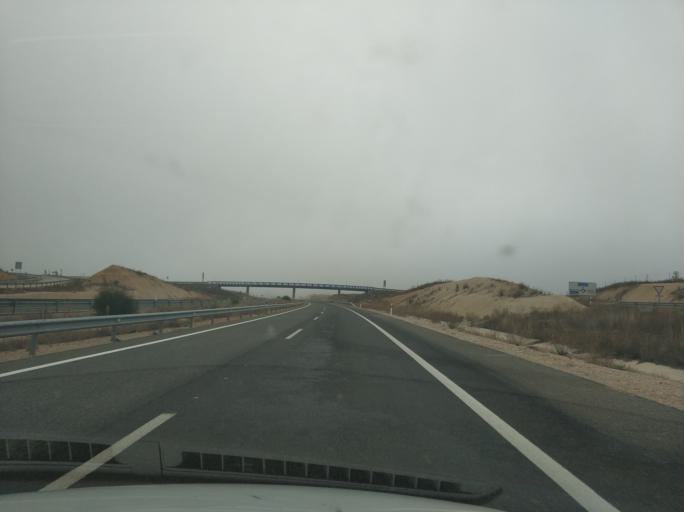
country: ES
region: Castille and Leon
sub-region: Provincia de Soria
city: Adradas
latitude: 41.3502
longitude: -2.4800
